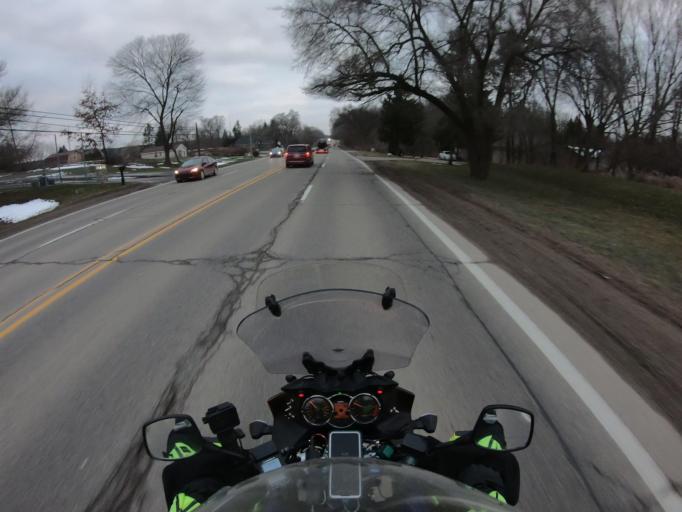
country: US
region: Michigan
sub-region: Oakland County
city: Clarkston
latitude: 42.7685
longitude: -83.4840
